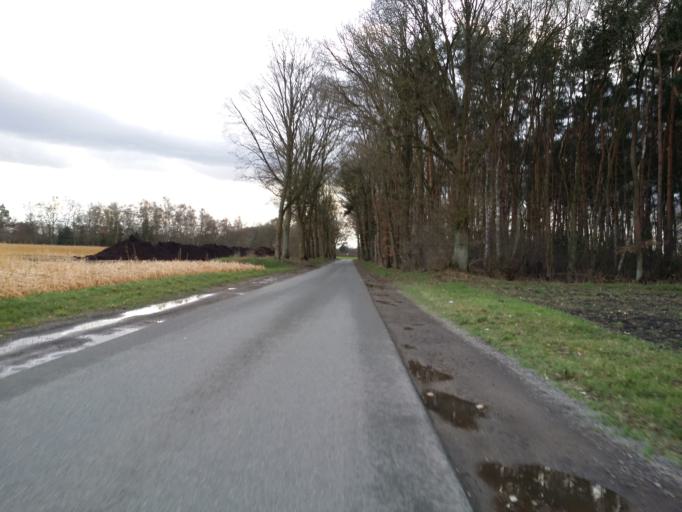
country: DE
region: Lower Saxony
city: Gross Ippener
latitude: 52.9908
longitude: 8.6365
